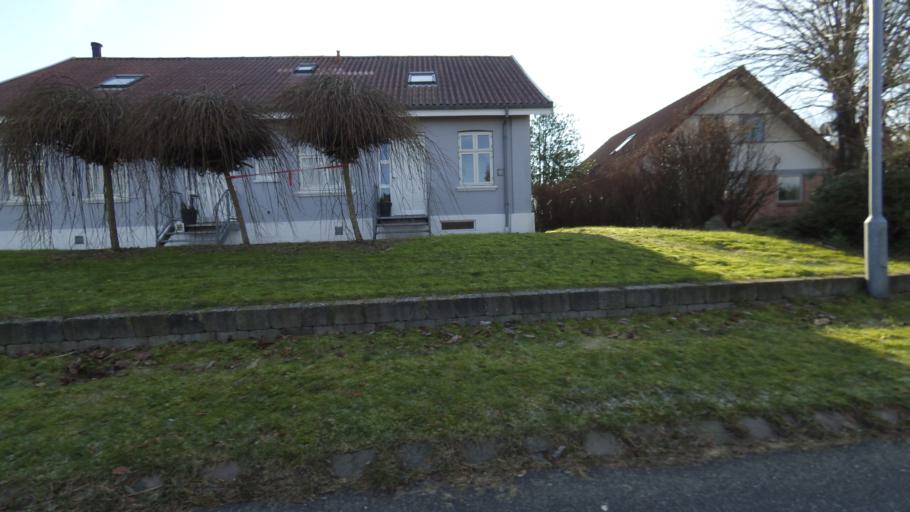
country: DK
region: Central Jutland
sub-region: Arhus Kommune
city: Kolt
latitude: 56.1081
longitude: 10.0873
